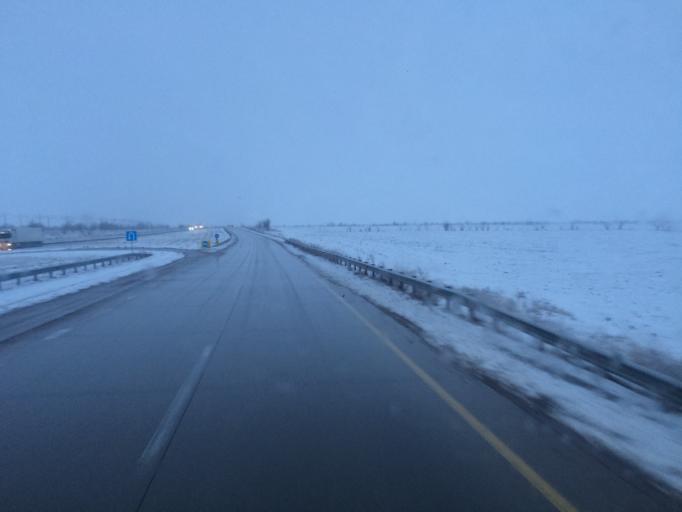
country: KZ
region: Zhambyl
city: Kulan
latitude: 42.9930
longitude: 72.3040
